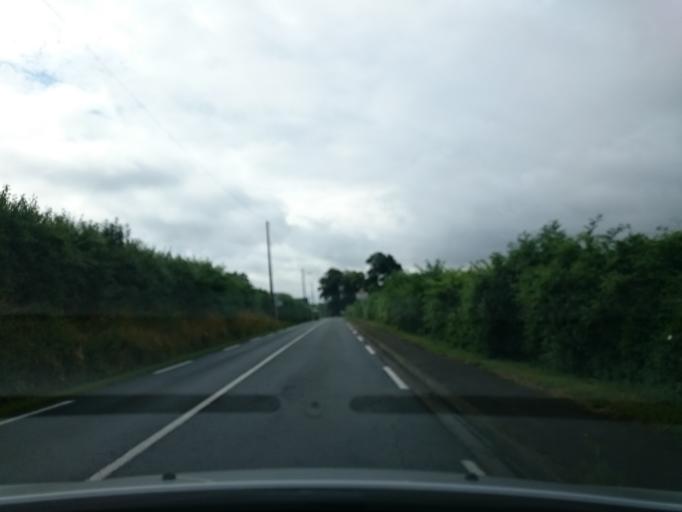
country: FR
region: Lower Normandy
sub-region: Departement du Calvados
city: Beuvillers
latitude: 49.1099
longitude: 0.2888
